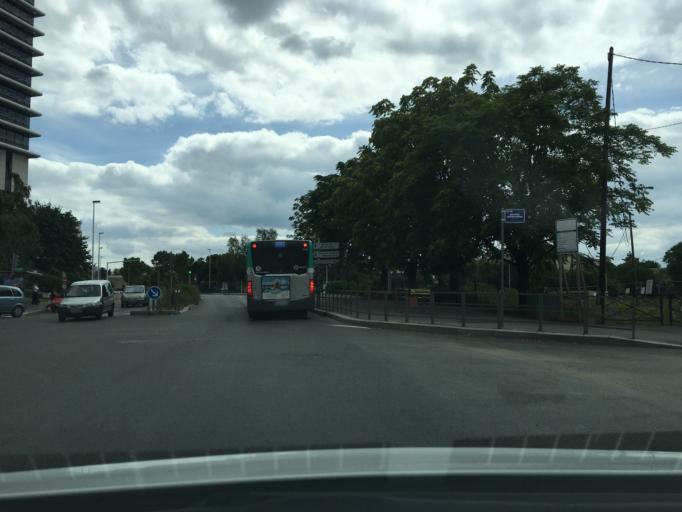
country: FR
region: Ile-de-France
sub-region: Departement des Hauts-de-Seine
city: Nanterre
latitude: 48.8990
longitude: 2.2138
